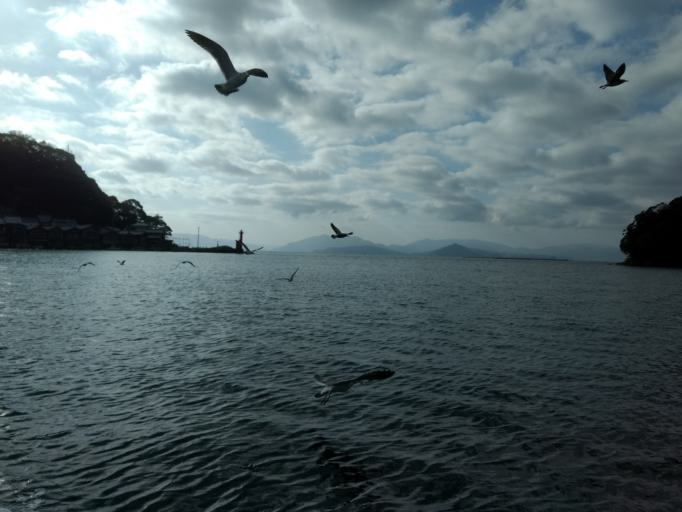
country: JP
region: Kyoto
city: Miyazu
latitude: 35.6673
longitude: 135.2874
